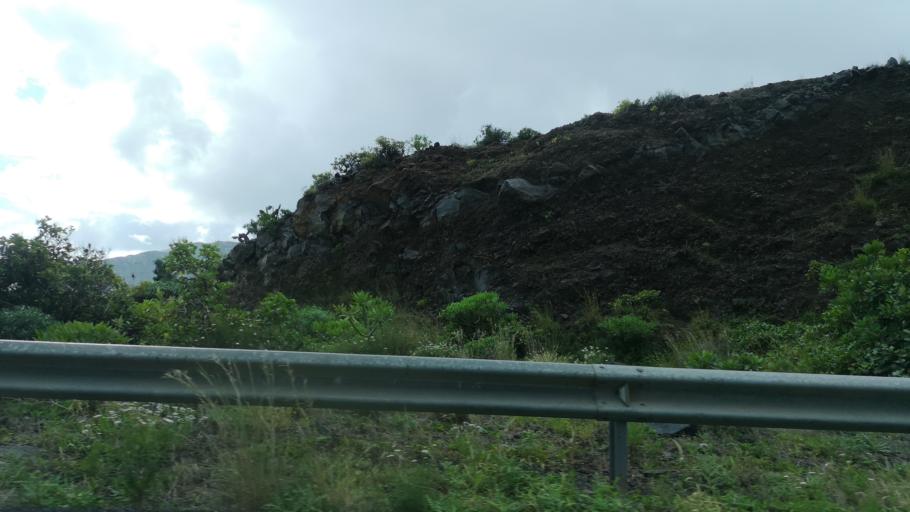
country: ES
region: Canary Islands
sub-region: Provincia de Santa Cruz de Tenerife
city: Hermigua
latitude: 28.1235
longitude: -17.1589
